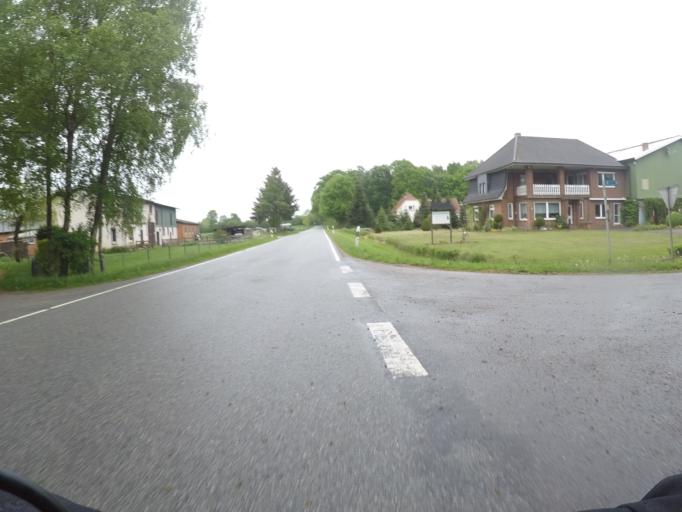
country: DE
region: Schleswig-Holstein
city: Rickling
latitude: 53.9758
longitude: 10.1362
